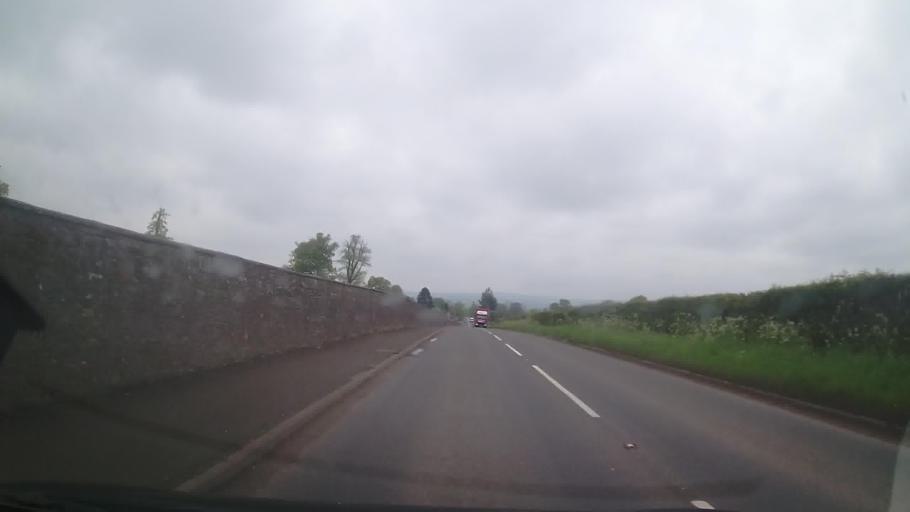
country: GB
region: Wales
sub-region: Wrexham
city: Ruabon
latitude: 52.9821
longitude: -3.0225
